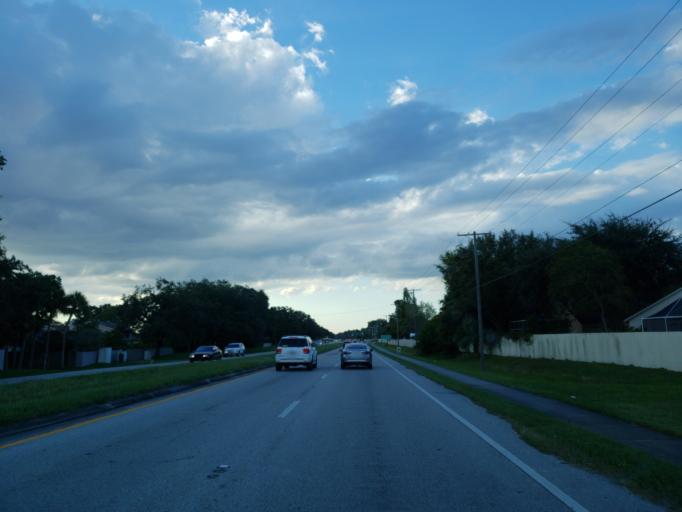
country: US
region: Florida
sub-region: Hillsborough County
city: Carrollwood Village
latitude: 28.0498
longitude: -82.5204
